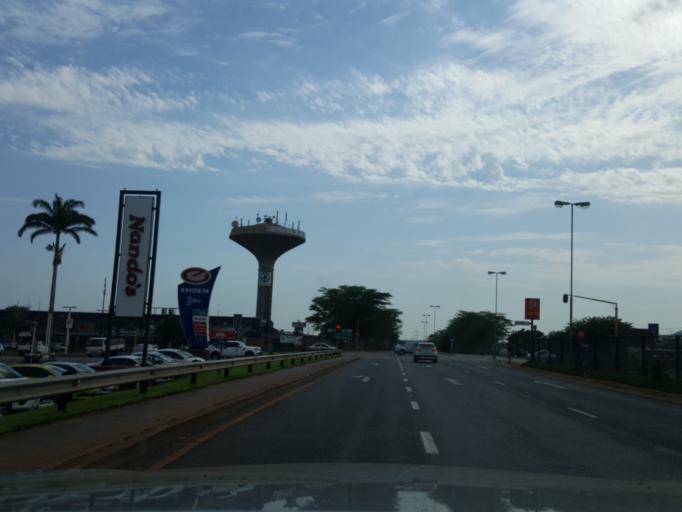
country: SZ
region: Hhohho
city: Ntfonjeni
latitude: -25.4999
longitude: 31.5080
